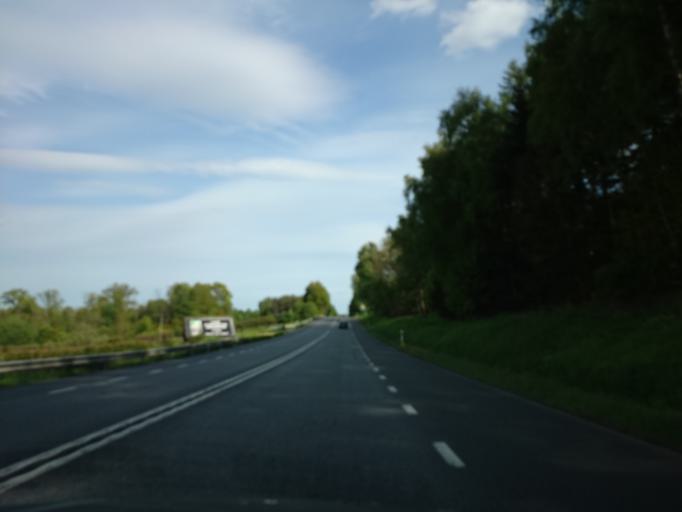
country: SE
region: Skane
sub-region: Kristianstads Kommun
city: Onnestad
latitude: 55.9354
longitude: 13.9161
